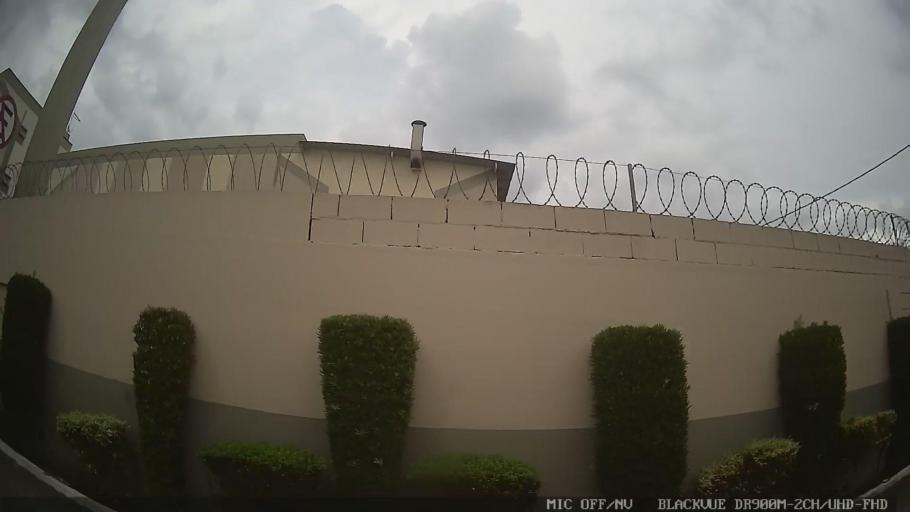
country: BR
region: Sao Paulo
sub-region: Suzano
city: Suzano
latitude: -23.5496
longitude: -46.3029
